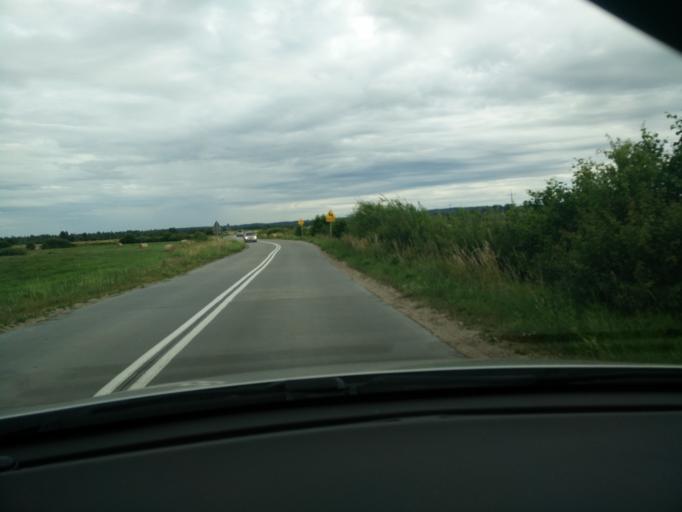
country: PL
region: Pomeranian Voivodeship
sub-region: Powiat pucki
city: Mrzezino
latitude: 54.6473
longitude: 18.4353
